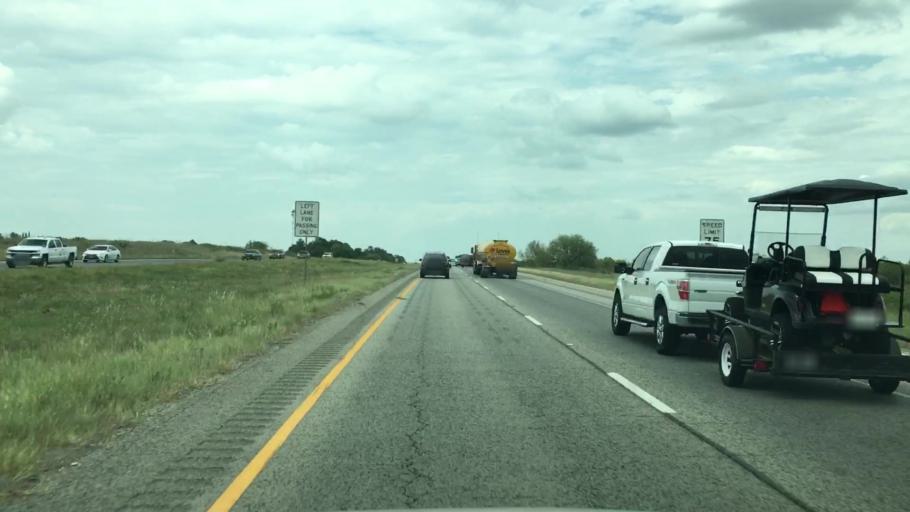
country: US
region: Texas
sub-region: Atascosa County
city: Poteet
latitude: 29.1171
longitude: -98.4316
